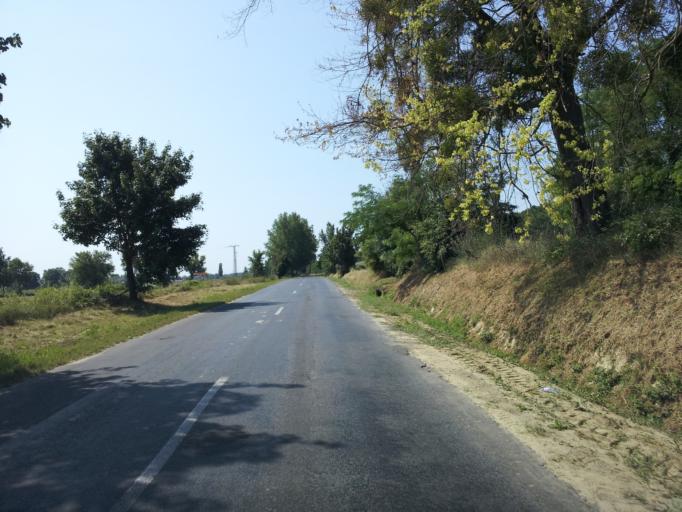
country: HU
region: Zala
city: Heviz
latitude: 46.8306
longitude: 17.0926
